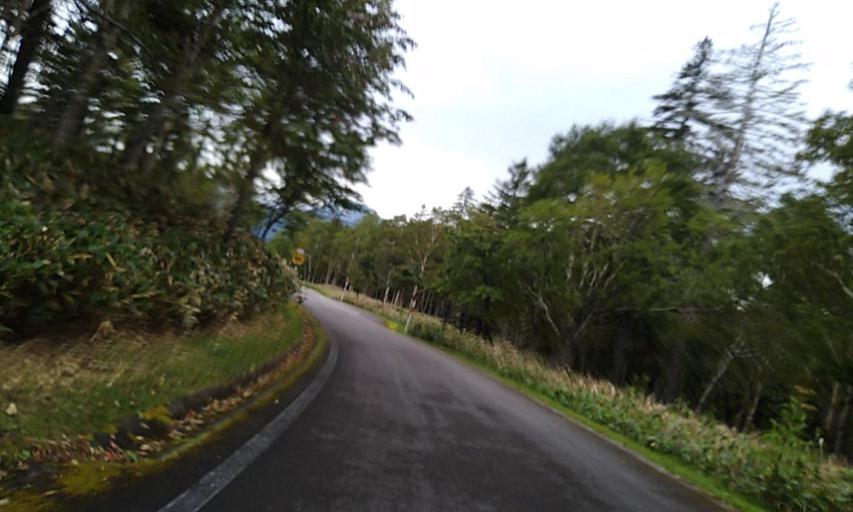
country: JP
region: Hokkaido
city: Bihoro
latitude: 43.5676
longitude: 144.2183
